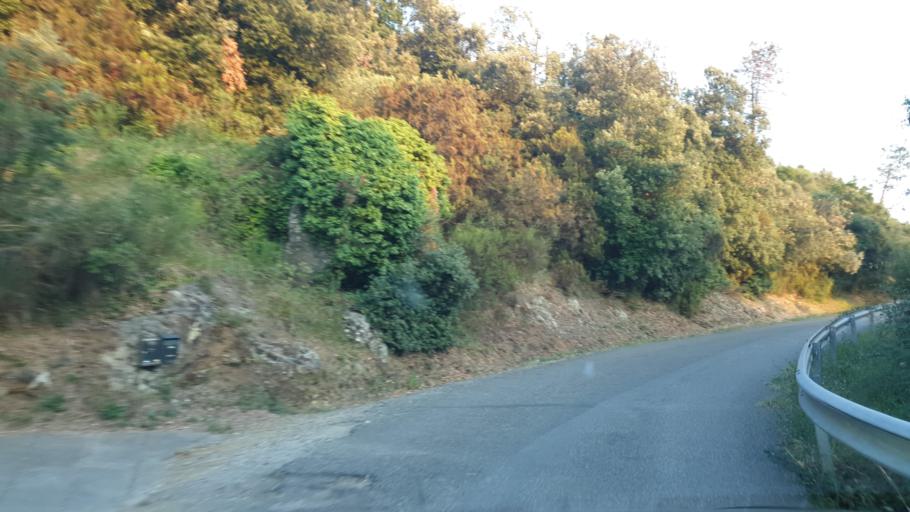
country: IT
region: Liguria
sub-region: Provincia di La Spezia
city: Bonassola
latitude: 44.1933
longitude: 9.5886
